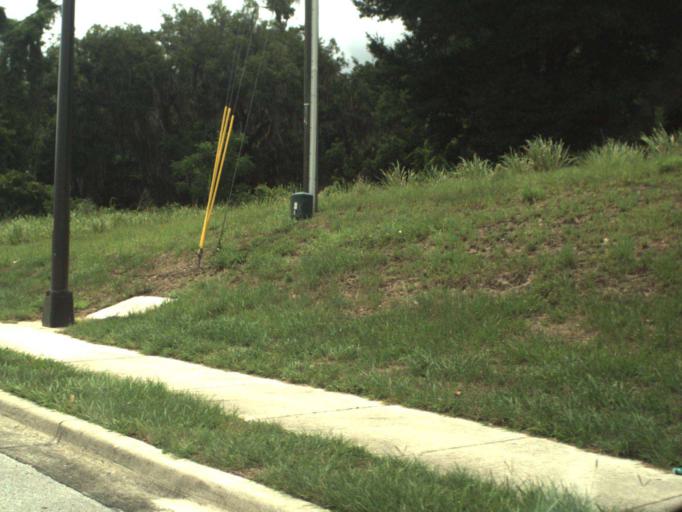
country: US
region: Florida
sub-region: Orange County
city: Apopka
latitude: 28.6732
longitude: -81.4966
